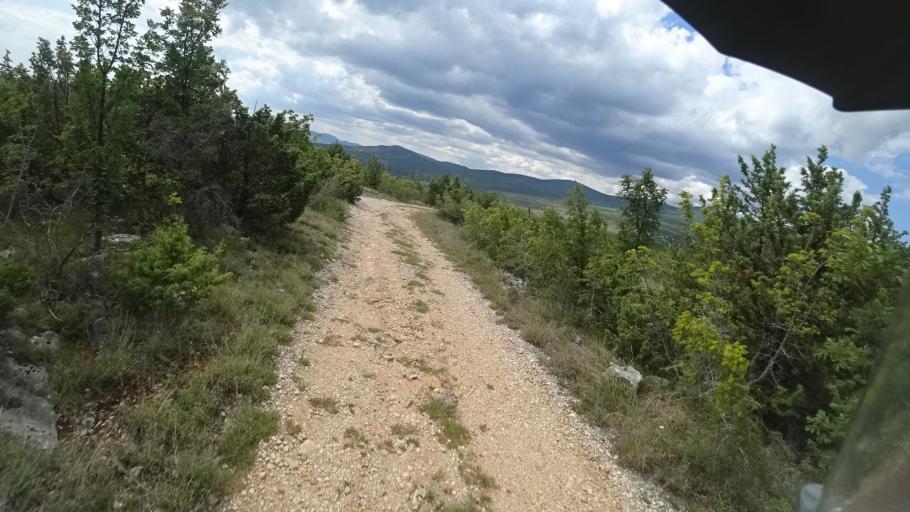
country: HR
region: Sibensko-Kniniska
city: Kistanje
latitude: 44.0887
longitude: 16.0534
